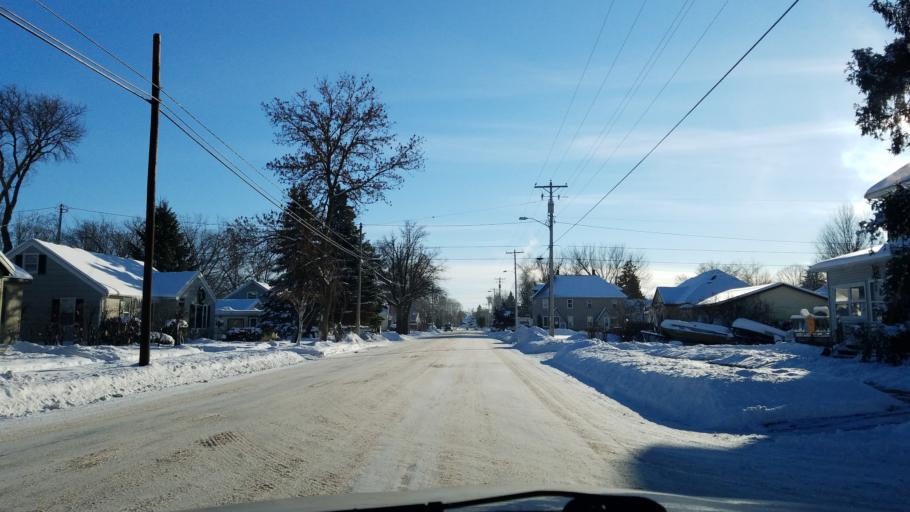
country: US
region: Wisconsin
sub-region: Barron County
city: Rice Lake
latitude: 45.5062
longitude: -91.7414
